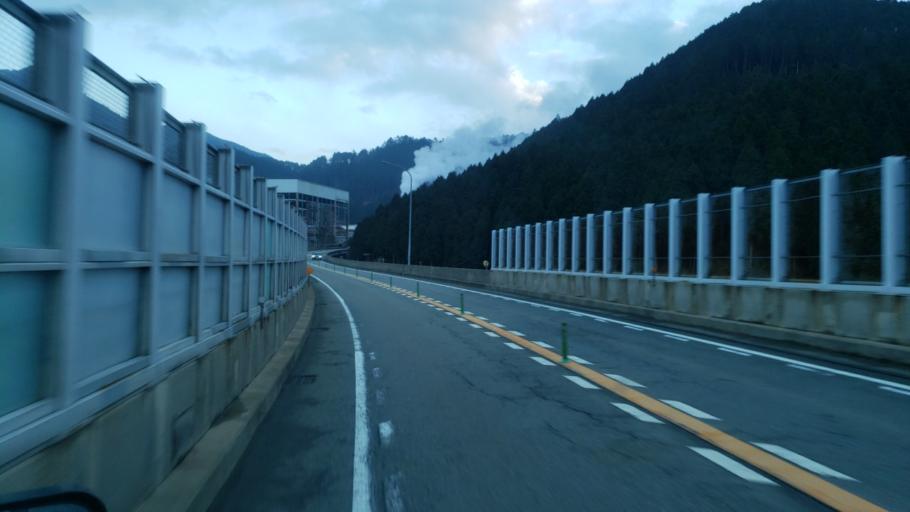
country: JP
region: Hyogo
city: Nishiwaki
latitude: 35.1502
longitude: 134.7869
